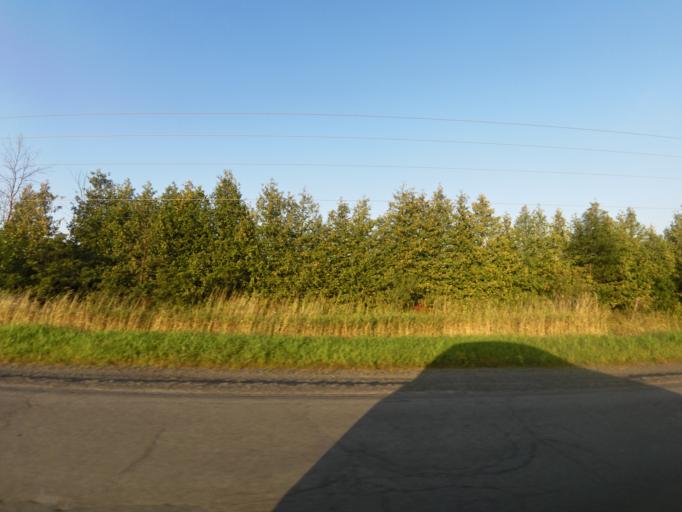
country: CA
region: Ontario
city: Clarence-Rockland
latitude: 45.4783
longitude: -75.4397
